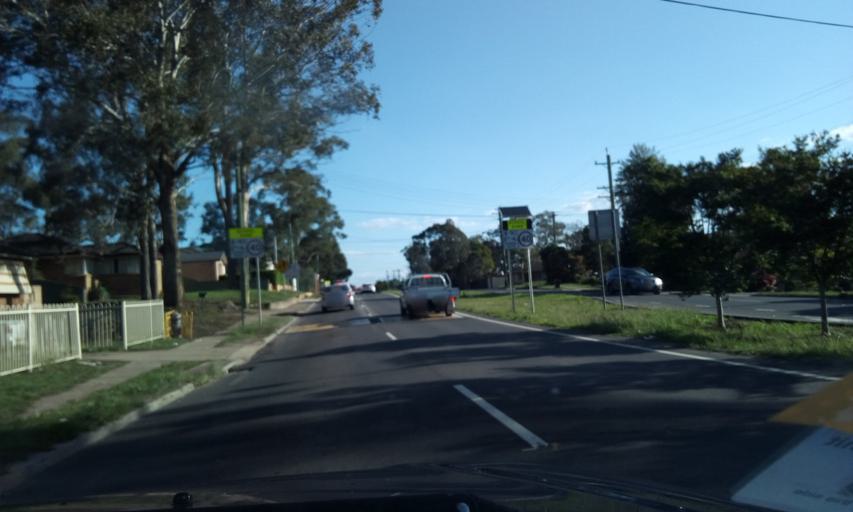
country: AU
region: New South Wales
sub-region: Penrith Municipality
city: Cambridge Park
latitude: -33.7519
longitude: 150.7134
